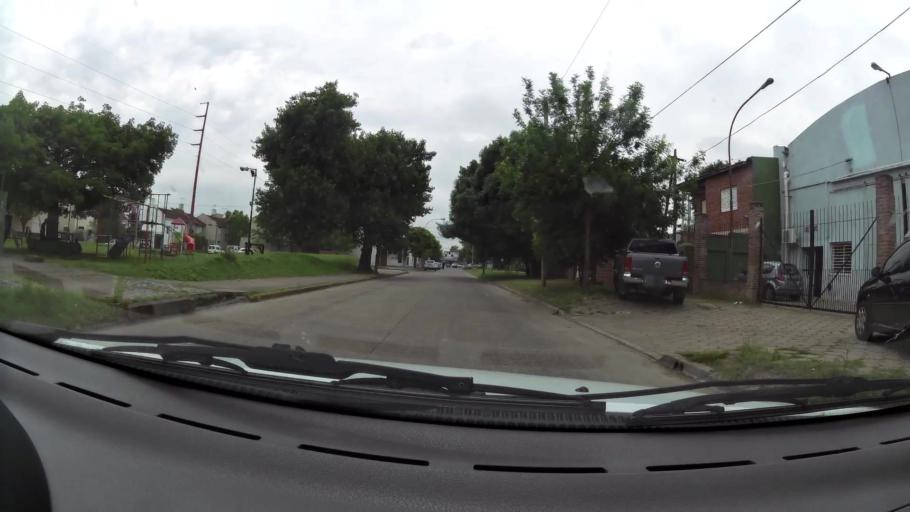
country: AR
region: Buenos Aires
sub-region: Partido de La Plata
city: La Plata
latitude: -34.9028
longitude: -57.9830
